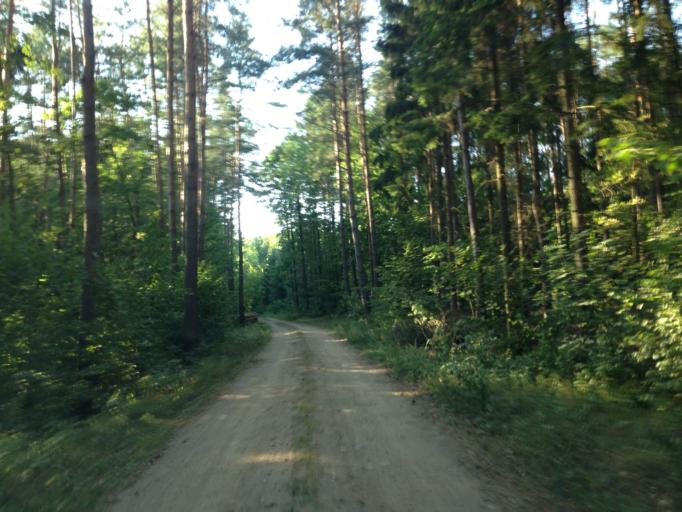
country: PL
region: Warmian-Masurian Voivodeship
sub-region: Powiat dzialdowski
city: Lidzbark
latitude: 53.2584
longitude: 19.7305
